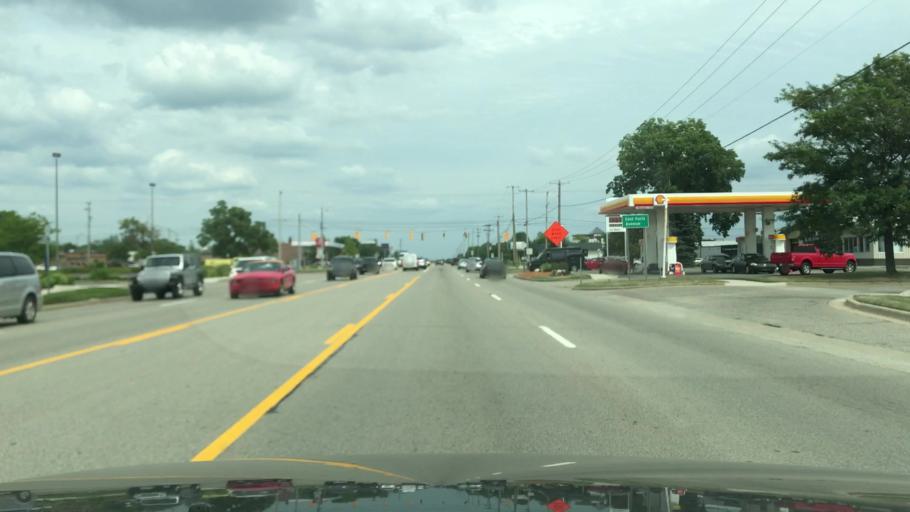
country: US
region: Michigan
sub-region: Kent County
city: East Grand Rapids
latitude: 42.9125
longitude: -85.5705
